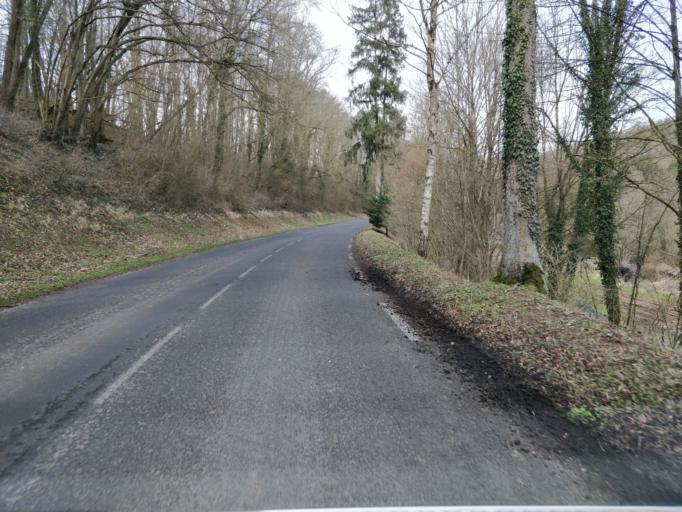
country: FR
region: Lorraine
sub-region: Departement de Meurthe-et-Moselle
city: Pagny-sur-Moselle
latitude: 48.9491
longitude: 5.8789
